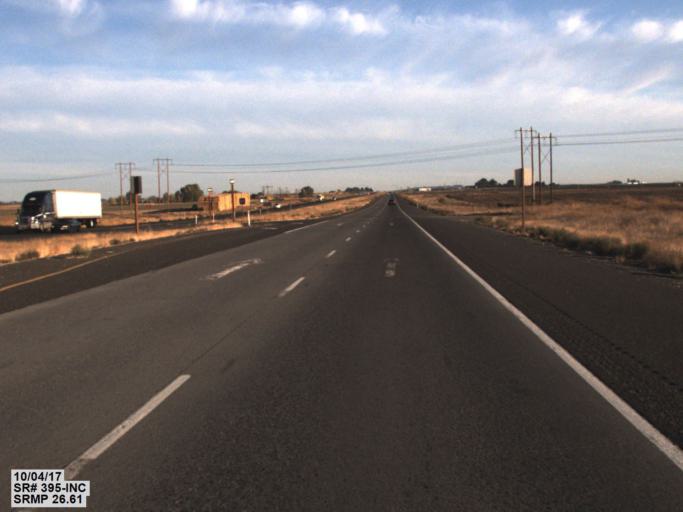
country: US
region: Washington
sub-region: Franklin County
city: Pasco
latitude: 46.3069
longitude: -119.0931
